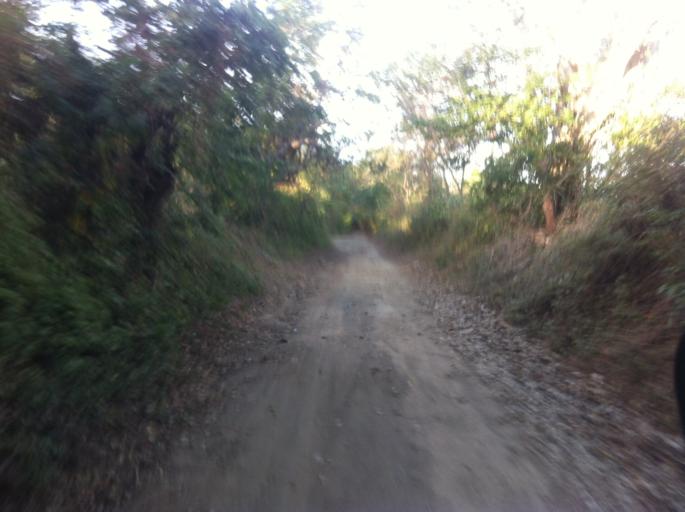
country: NI
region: Managua
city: Managua
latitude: 12.0742
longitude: -86.3103
